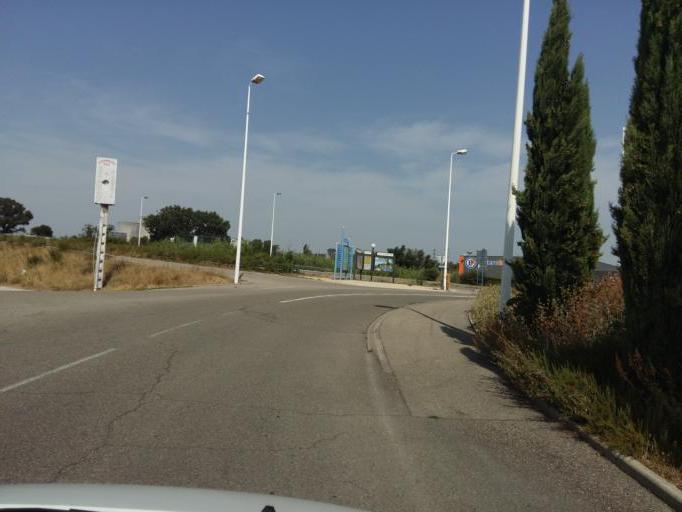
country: FR
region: Rhone-Alpes
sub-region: Departement de la Drome
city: Saint-Paul-Trois-Chateaux
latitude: 44.3233
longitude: 4.7414
